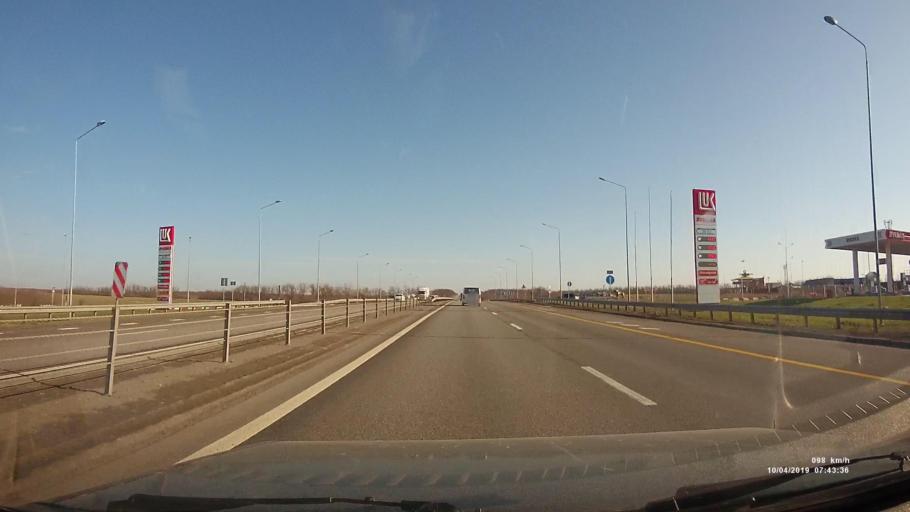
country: RU
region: Rostov
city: Likhoy
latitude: 48.1654
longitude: 40.2629
